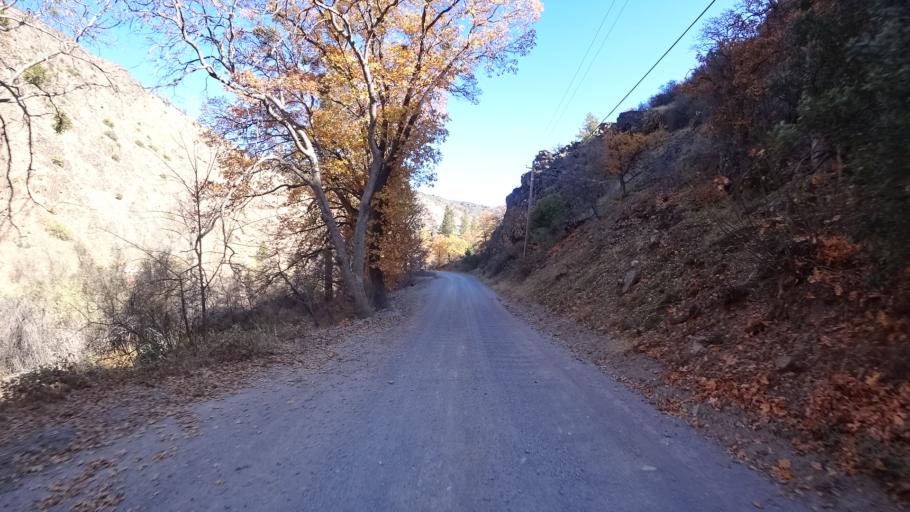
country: US
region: California
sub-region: Siskiyou County
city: Yreka
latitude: 41.8321
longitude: -122.6253
